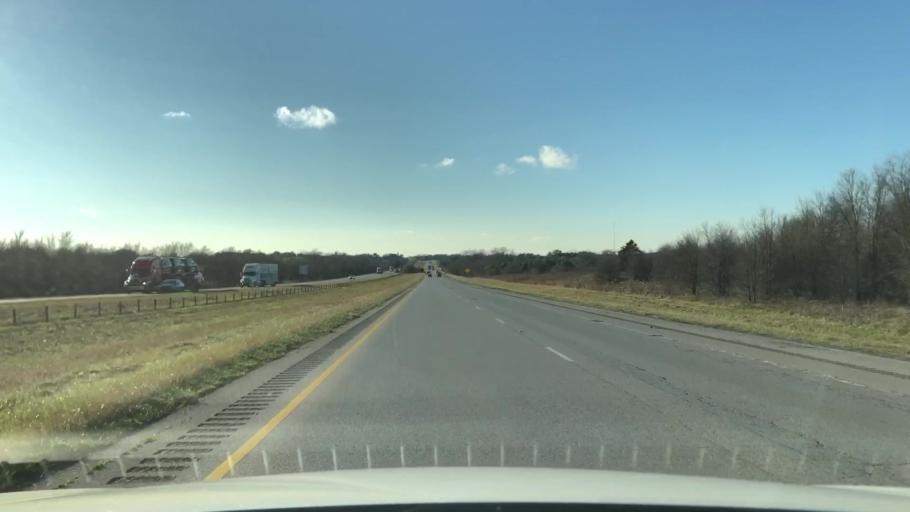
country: US
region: Texas
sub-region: Fayette County
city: Schulenburg
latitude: 29.6965
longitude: -96.8655
